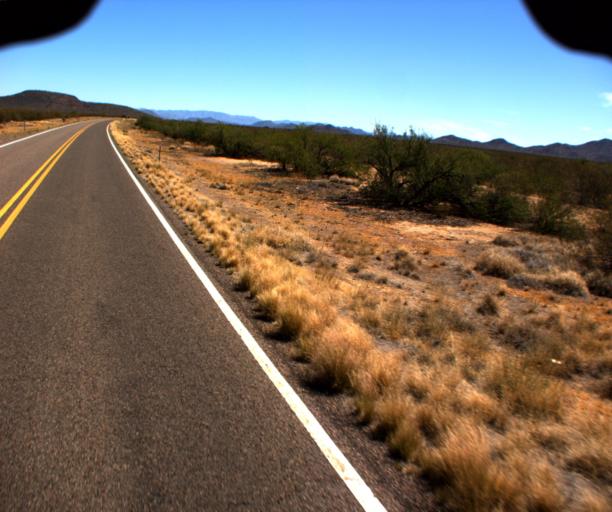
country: US
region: Arizona
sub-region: Yavapai County
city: Congress
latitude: 33.9901
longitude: -113.1336
